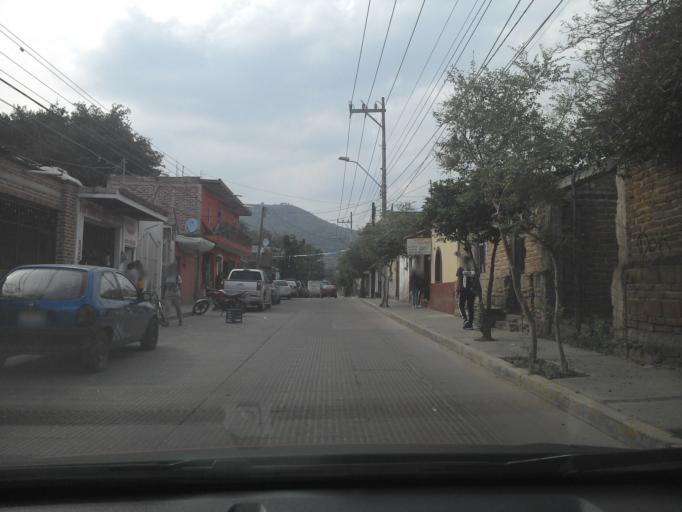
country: MX
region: Jalisco
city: Tlajomulco de Zuniga
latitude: 20.4777
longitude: -103.4485
